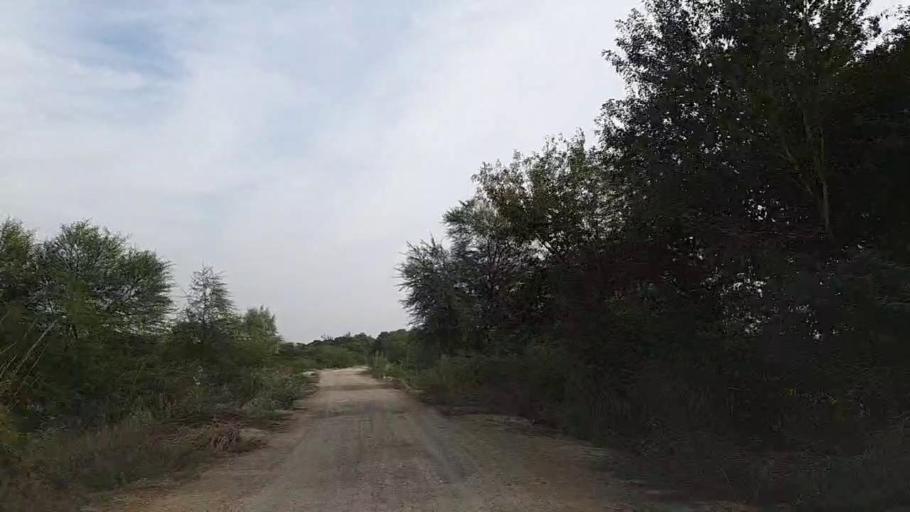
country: PK
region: Sindh
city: Jam Sahib
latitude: 26.4374
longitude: 68.6297
